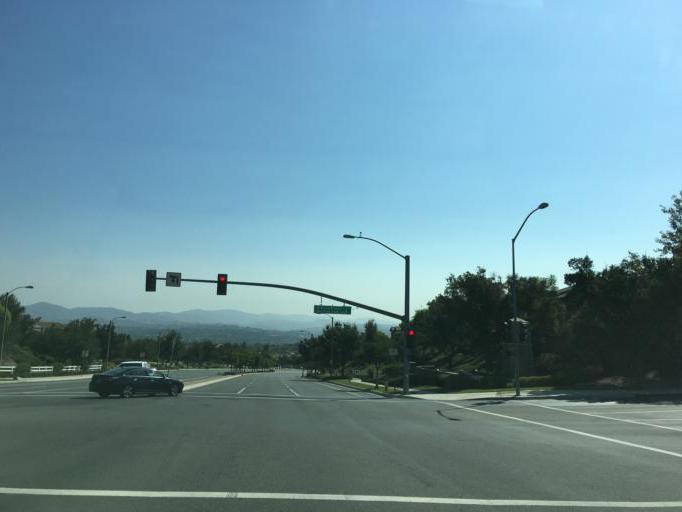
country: US
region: California
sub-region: Los Angeles County
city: Valencia
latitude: 34.4056
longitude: -118.5862
